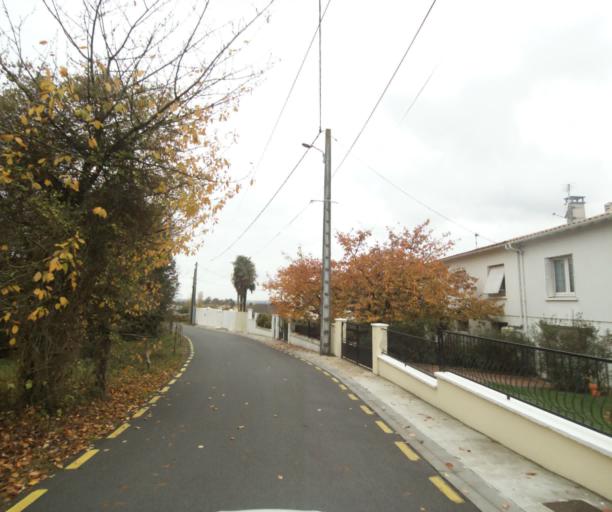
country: FR
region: Poitou-Charentes
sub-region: Departement de la Charente-Maritime
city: Saintes
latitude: 45.7489
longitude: -0.6071
